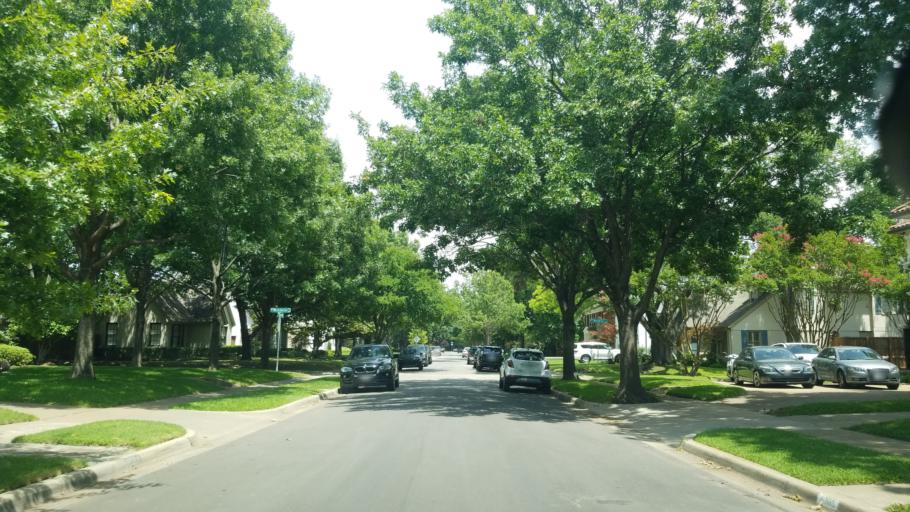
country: US
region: Texas
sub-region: Dallas County
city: University Park
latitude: 32.8531
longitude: -96.8070
